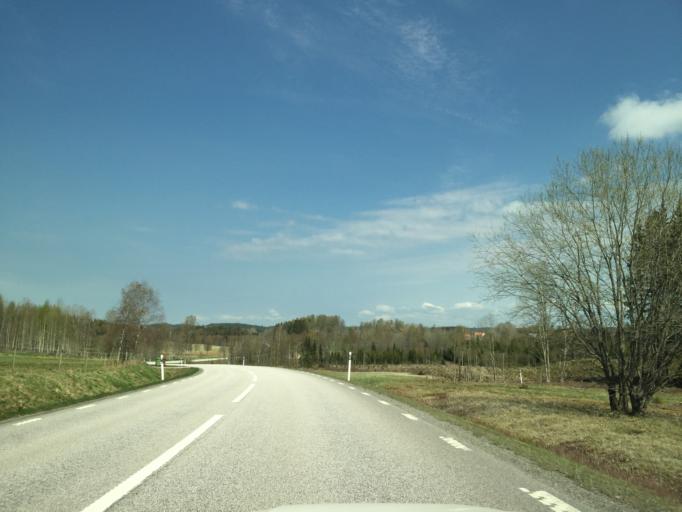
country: SE
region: Vaestra Goetaland
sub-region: Bengtsfors Kommun
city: Dals Langed
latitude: 58.8590
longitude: 12.1842
